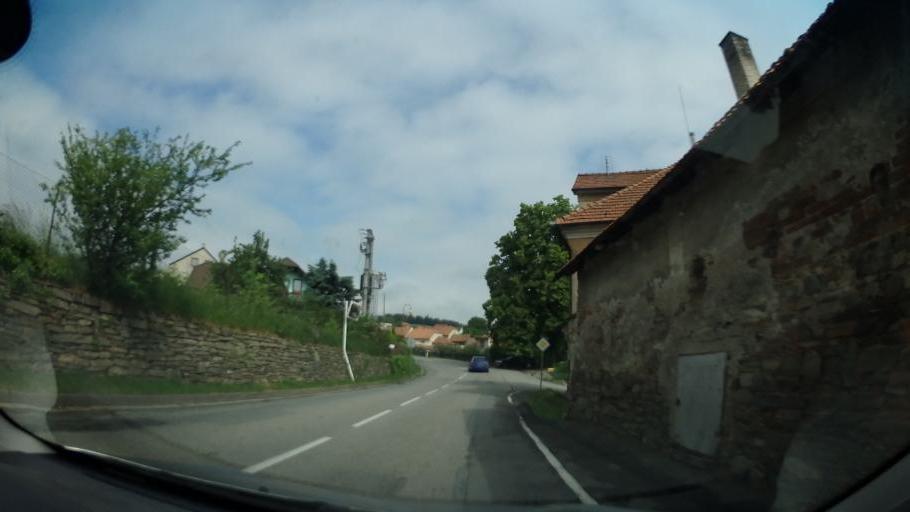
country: CZ
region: South Moravian
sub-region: Okres Brno-Venkov
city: Dolni Loucky
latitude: 49.3780
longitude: 16.3525
